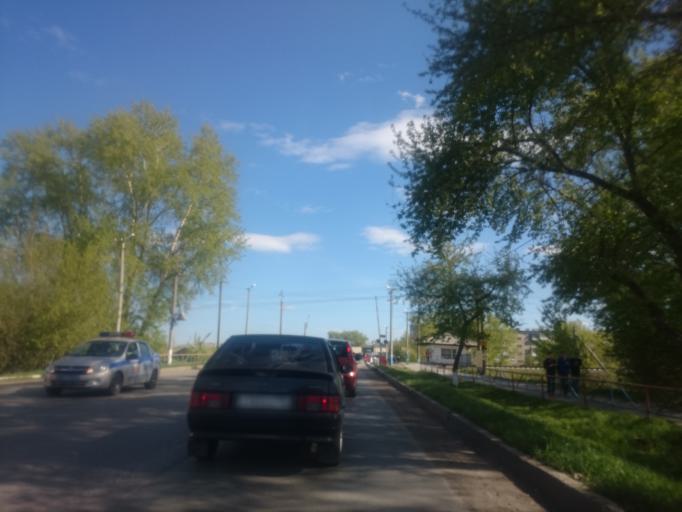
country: RU
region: Sverdlovsk
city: Irbit
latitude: 57.6697
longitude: 63.0744
